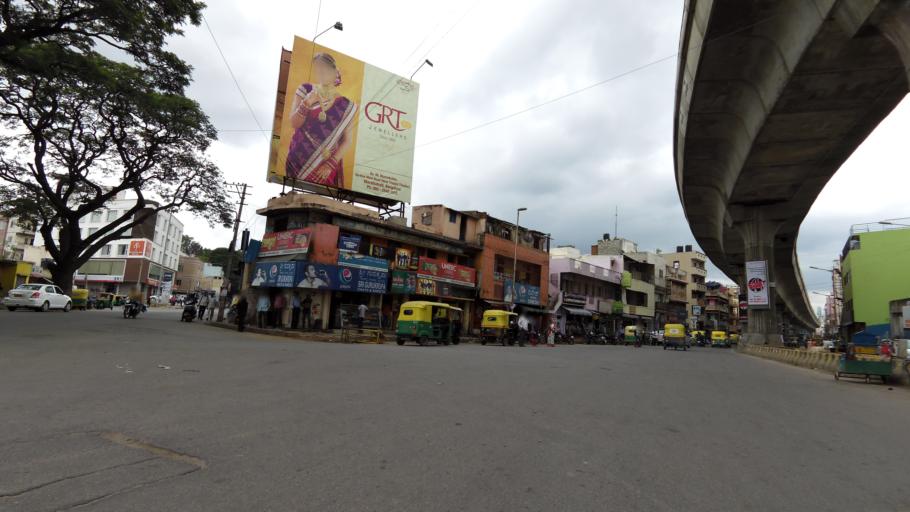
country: IN
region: Karnataka
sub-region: Bangalore Urban
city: Bangalore
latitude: 12.9784
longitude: 77.6288
